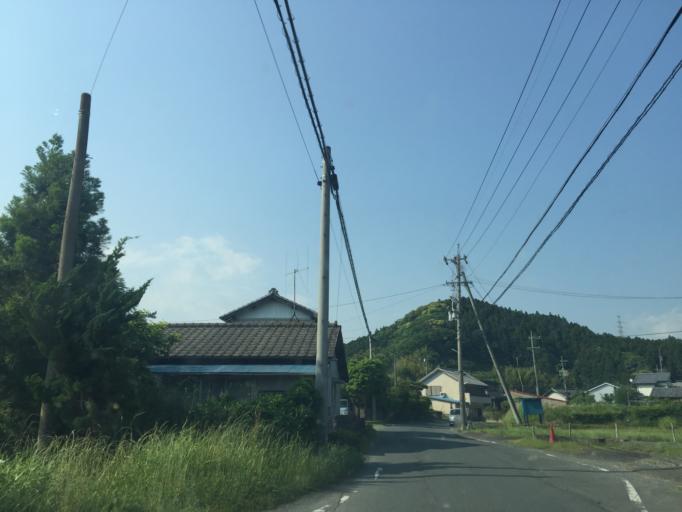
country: JP
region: Shizuoka
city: Kakegawa
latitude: 34.8203
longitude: 138.0340
